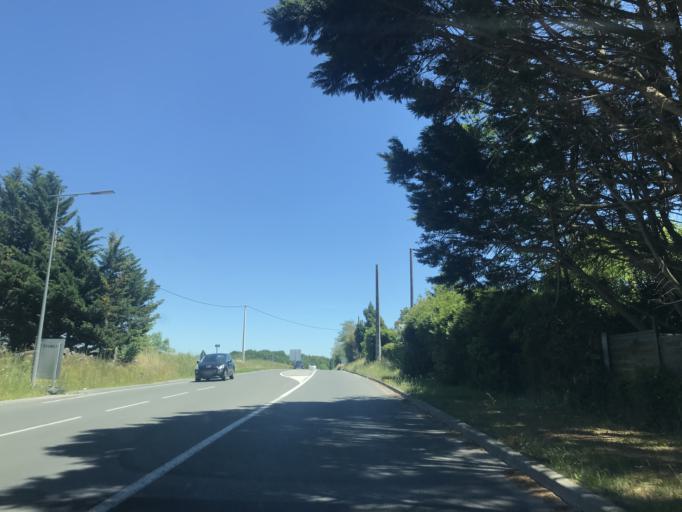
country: FR
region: Poitou-Charentes
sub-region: Departement de la Charente-Maritime
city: Vaux-sur-Mer
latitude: 45.6636
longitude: -1.0711
